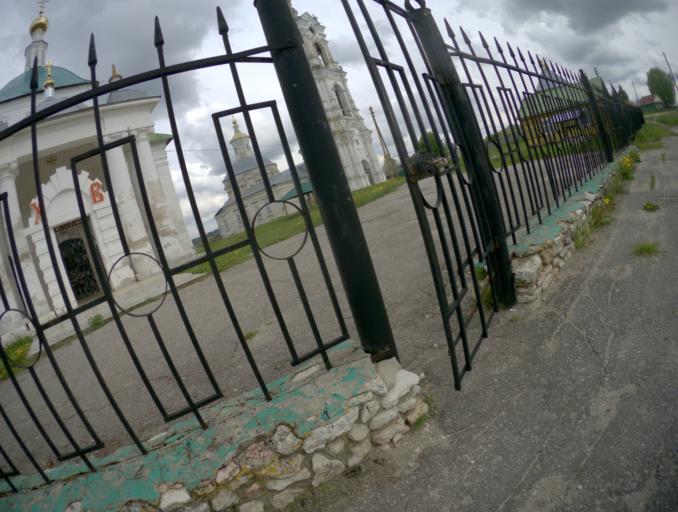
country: RU
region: Rjazan
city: Gus'-Zheleznyy
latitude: 55.0097
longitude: 41.1602
